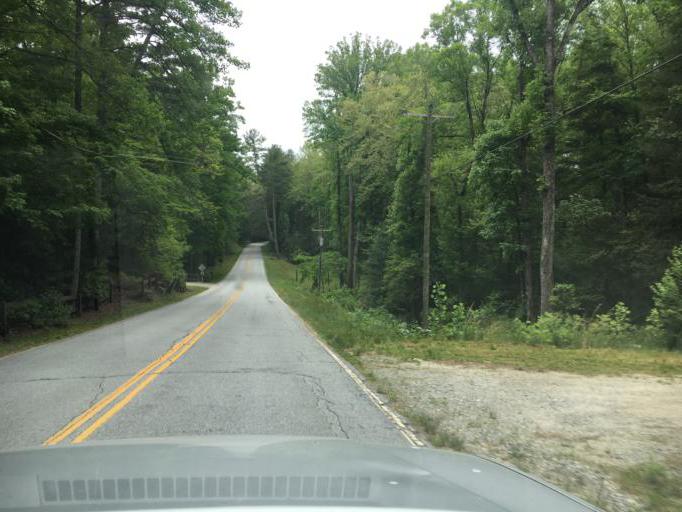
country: US
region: North Carolina
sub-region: Henderson County
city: Flat Rock
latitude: 35.2086
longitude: -82.4378
